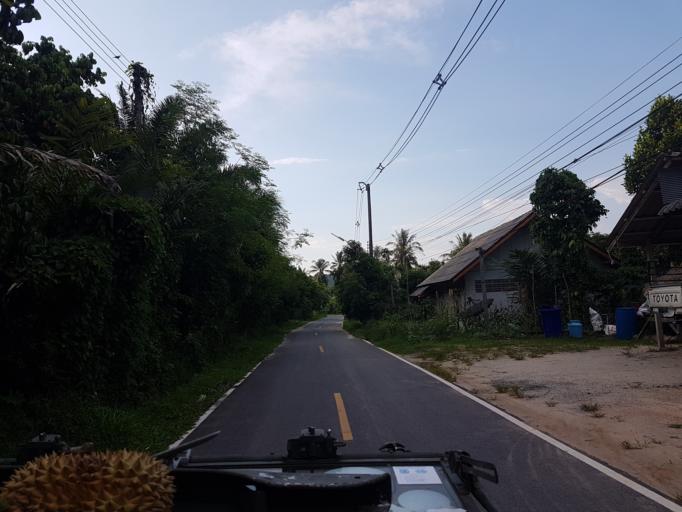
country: TH
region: Pattani
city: Khok Pho
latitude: 6.6738
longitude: 101.0950
